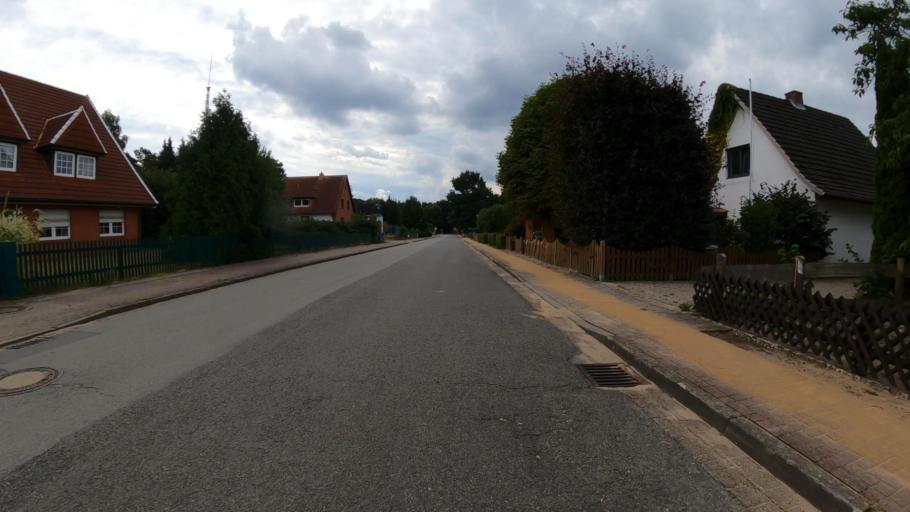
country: DE
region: Lower Saxony
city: Drestedt
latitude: 53.3309
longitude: 9.7564
